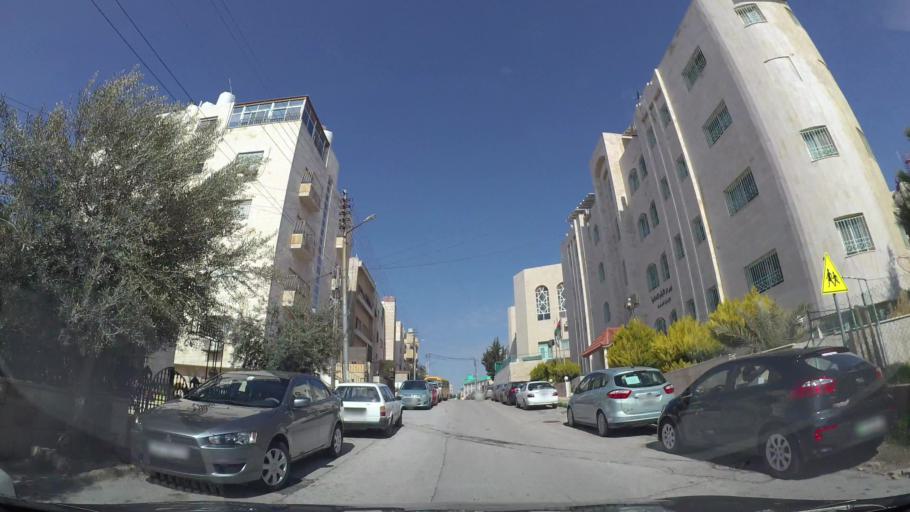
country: JO
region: Amman
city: Al Jubayhah
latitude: 31.9976
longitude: 35.8954
